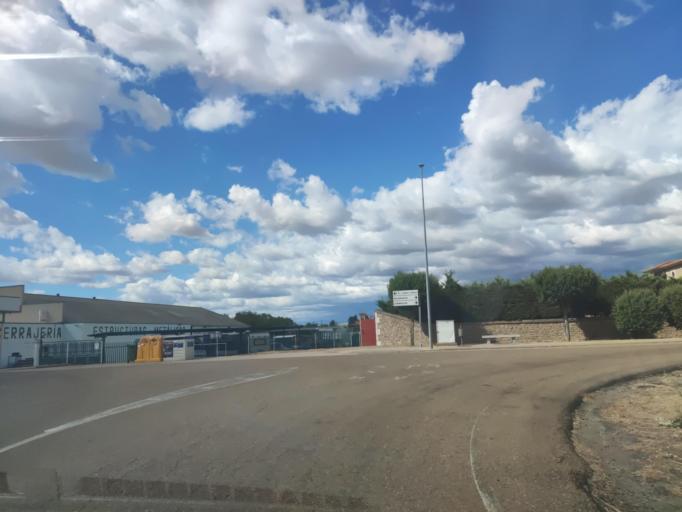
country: ES
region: Castille and Leon
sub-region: Provincia de Salamanca
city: Vitigudino
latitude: 41.0085
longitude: -6.4262
